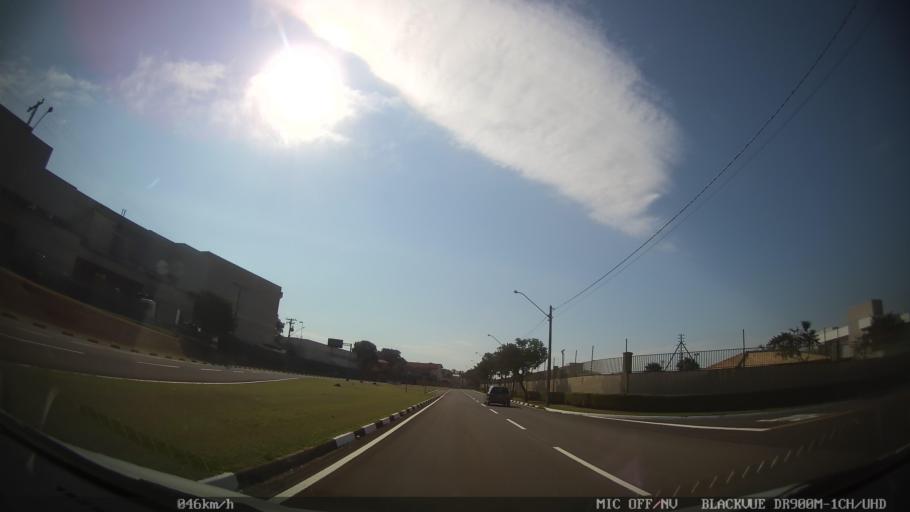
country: BR
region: Sao Paulo
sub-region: Paulinia
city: Paulinia
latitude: -22.7808
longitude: -47.1525
